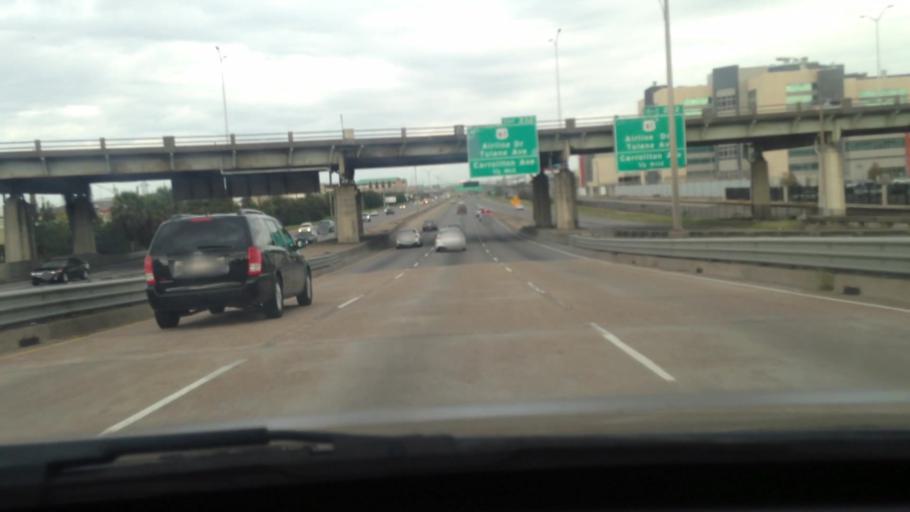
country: US
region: Louisiana
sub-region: Orleans Parish
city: New Orleans
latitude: 29.9574
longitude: -90.0935
